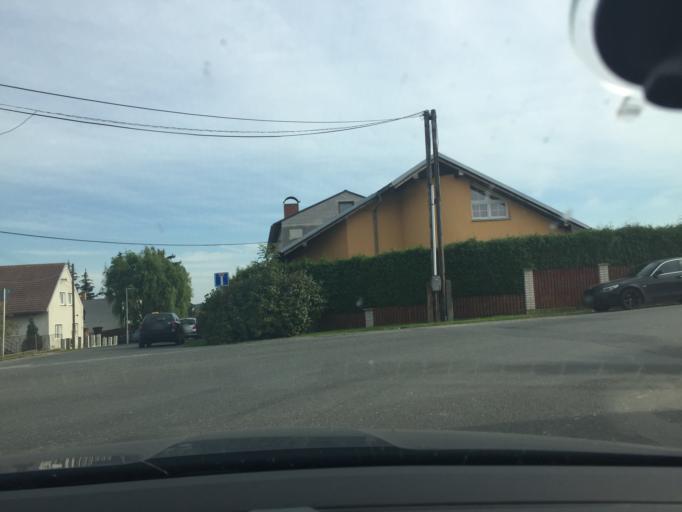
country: CZ
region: Central Bohemia
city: Cirkvice
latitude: 49.9680
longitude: 15.3074
